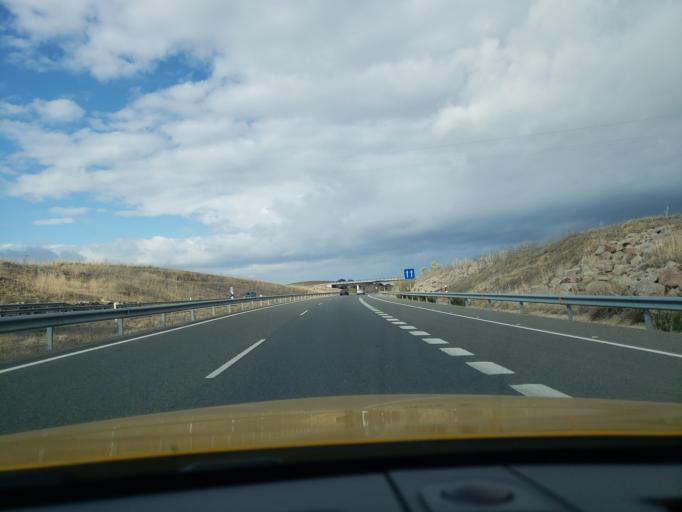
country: ES
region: Andalusia
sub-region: Provincia de Jaen
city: Mengibar
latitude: 37.9134
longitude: -3.7877
